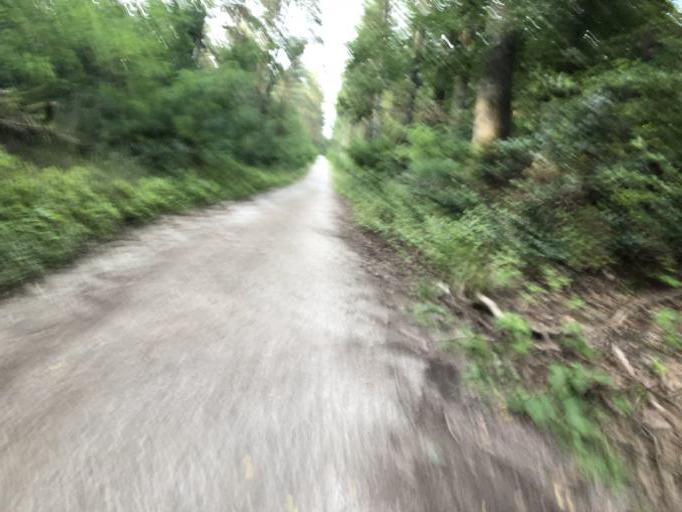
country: DE
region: Bavaria
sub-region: Regierungsbezirk Mittelfranken
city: Uttenreuth
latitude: 49.5658
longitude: 11.0752
